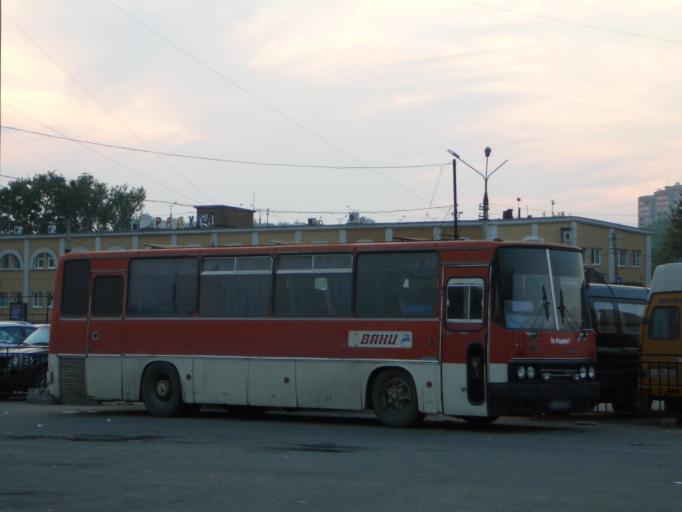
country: RU
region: Smolensk
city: Smolensk
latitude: 54.7944
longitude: 32.0483
